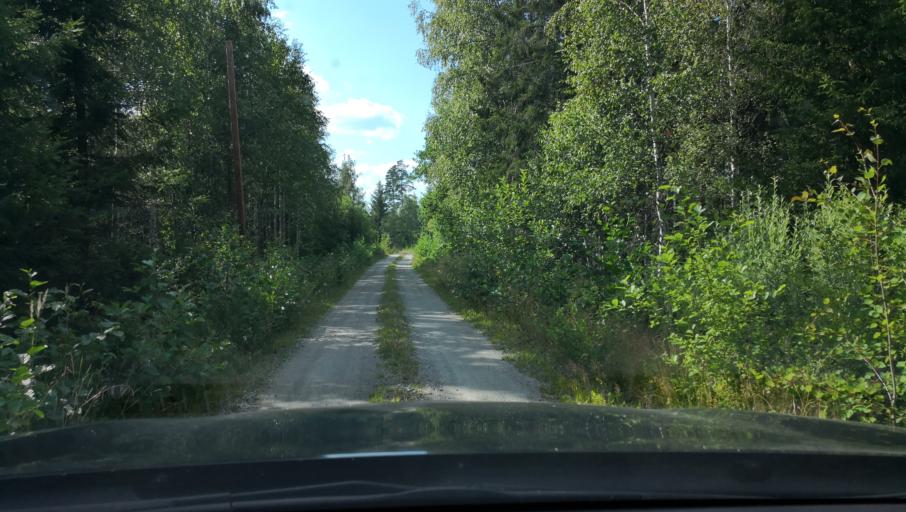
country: SE
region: Vaestmanland
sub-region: Vasteras
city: Skultuna
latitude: 59.7260
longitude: 16.3709
